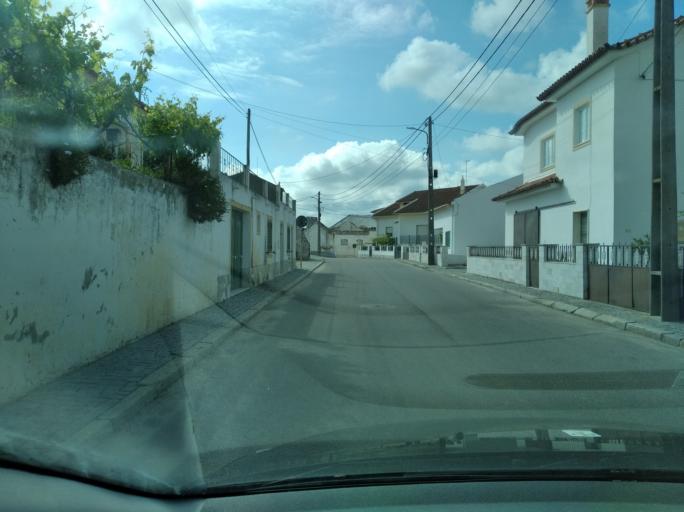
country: PT
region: Portalegre
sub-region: Avis
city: Avis
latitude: 39.0547
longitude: -7.8927
